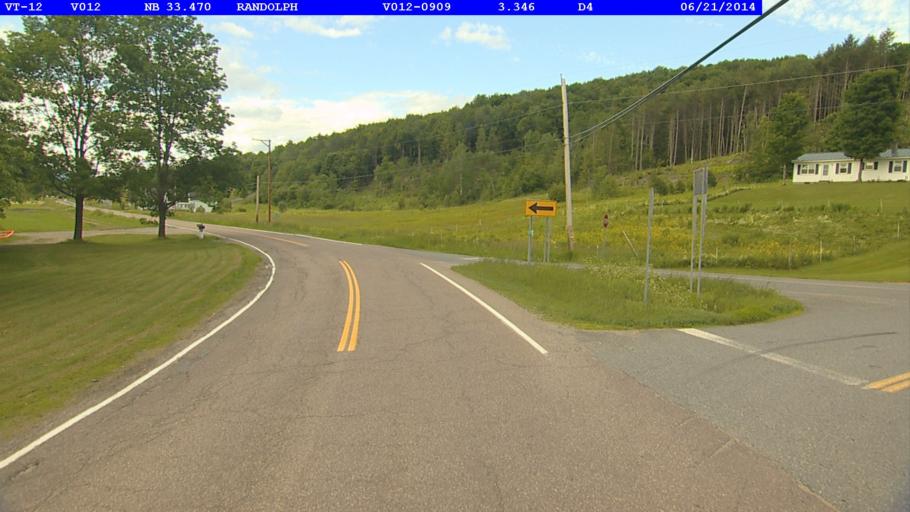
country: US
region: Vermont
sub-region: Orange County
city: Randolph
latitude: 43.9372
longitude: -72.6545
